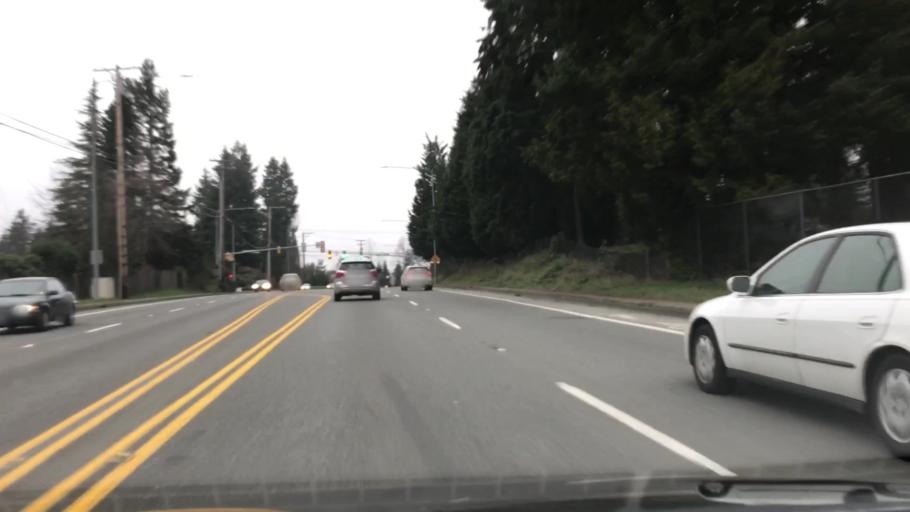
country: US
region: Washington
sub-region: King County
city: Fairwood
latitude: 47.4545
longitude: -122.1538
